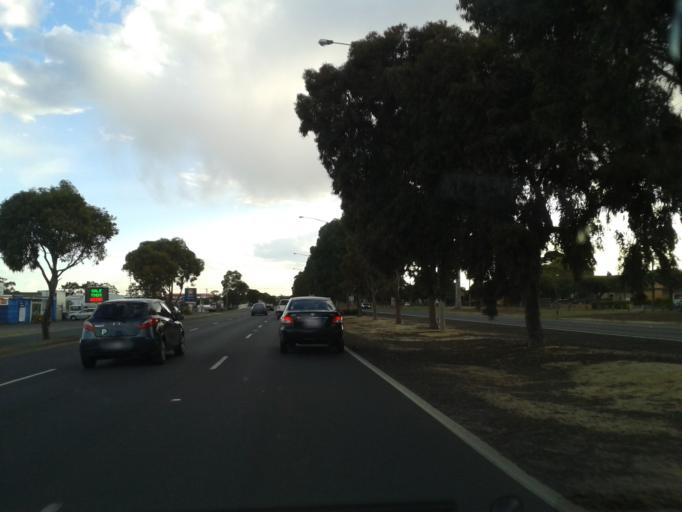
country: AU
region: Victoria
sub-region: Greater Geelong
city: Bell Park
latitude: -38.0765
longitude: 144.3677
